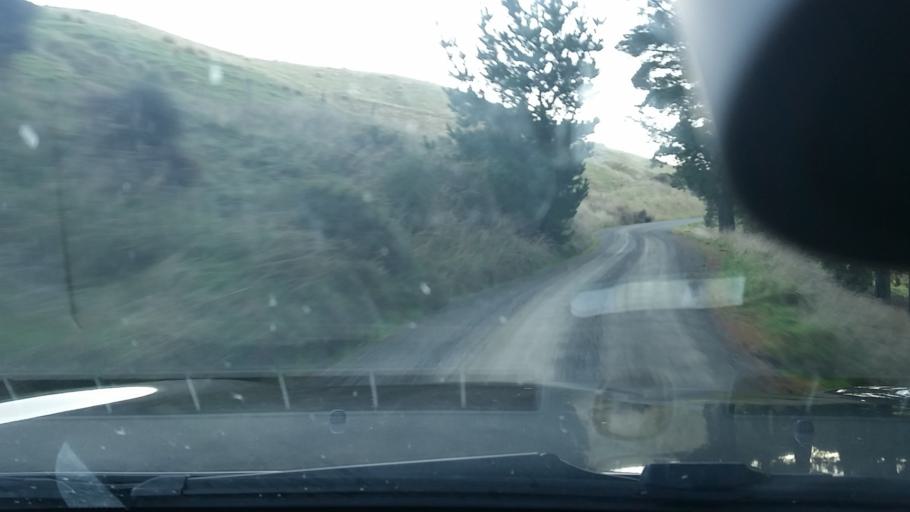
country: NZ
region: Marlborough
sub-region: Marlborough District
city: Blenheim
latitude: -41.7499
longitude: 174.0590
